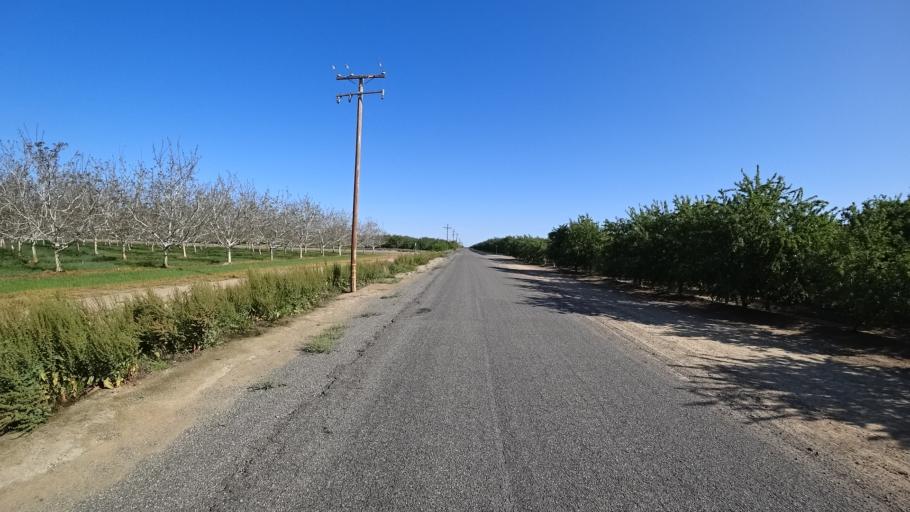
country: US
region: California
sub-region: Glenn County
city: Hamilton City
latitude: 39.6939
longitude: -122.0641
